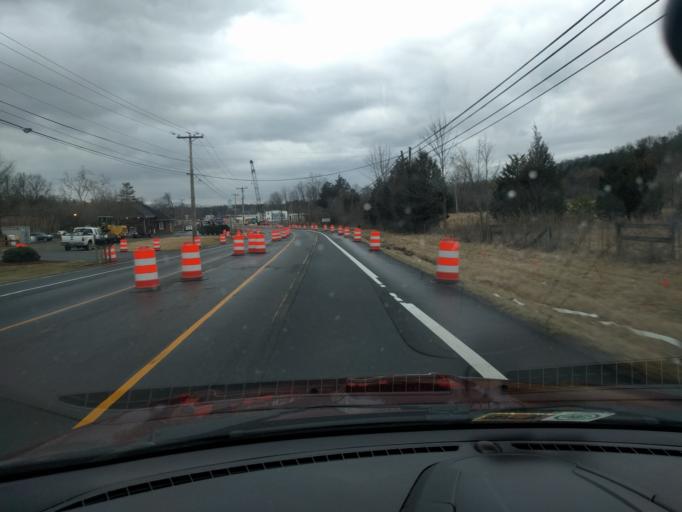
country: US
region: Virginia
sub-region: Botetourt County
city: Cloverdale
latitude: 37.3629
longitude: -79.9207
